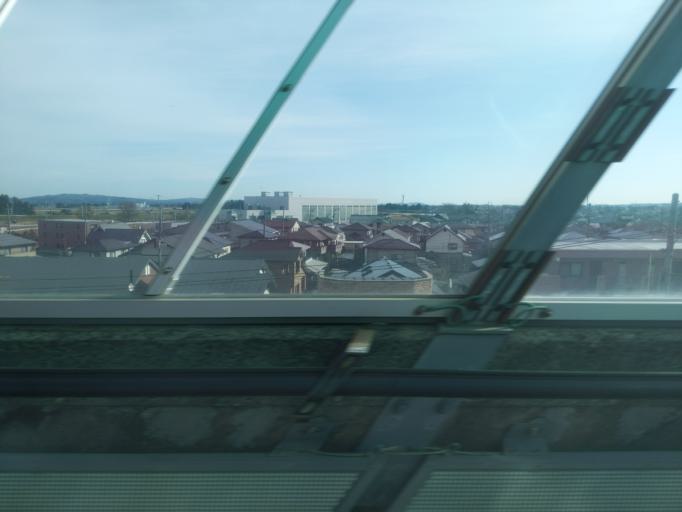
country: JP
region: Miyagi
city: Furukawa
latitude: 38.5846
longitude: 140.9720
